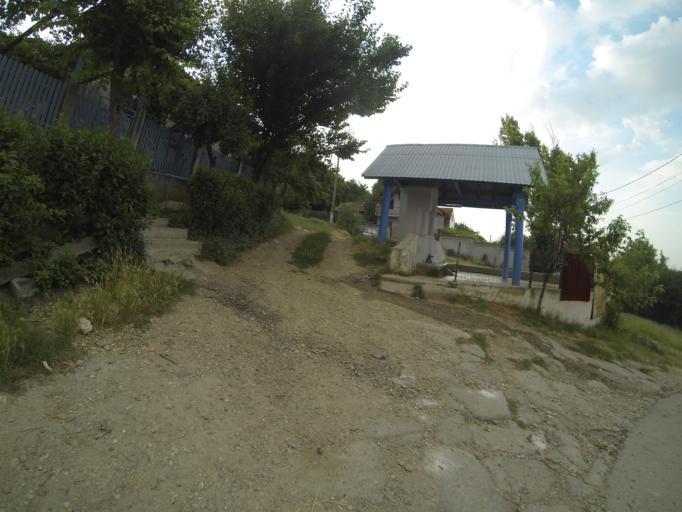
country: RO
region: Dolj
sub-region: Comuna Tuglui
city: Tuglui
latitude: 44.2061
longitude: 23.7951
